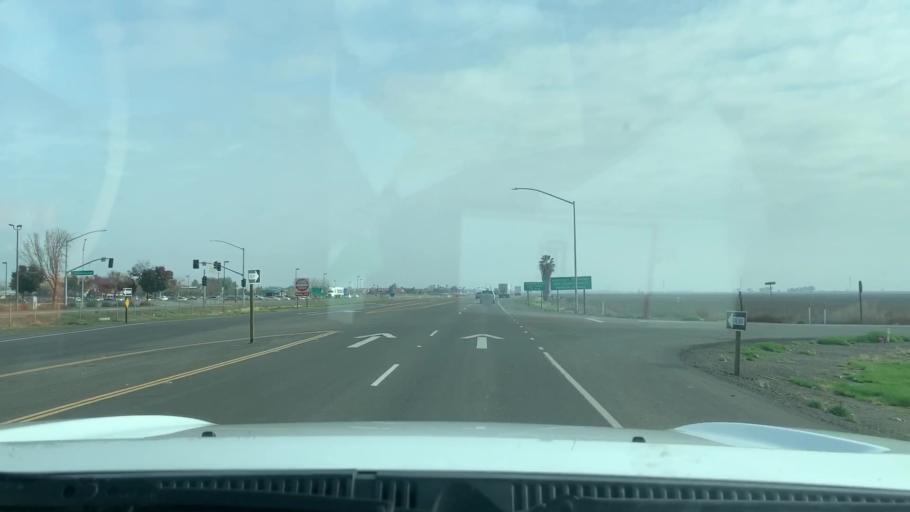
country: US
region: California
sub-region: Kings County
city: Lemoore Station
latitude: 36.2553
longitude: -119.9053
